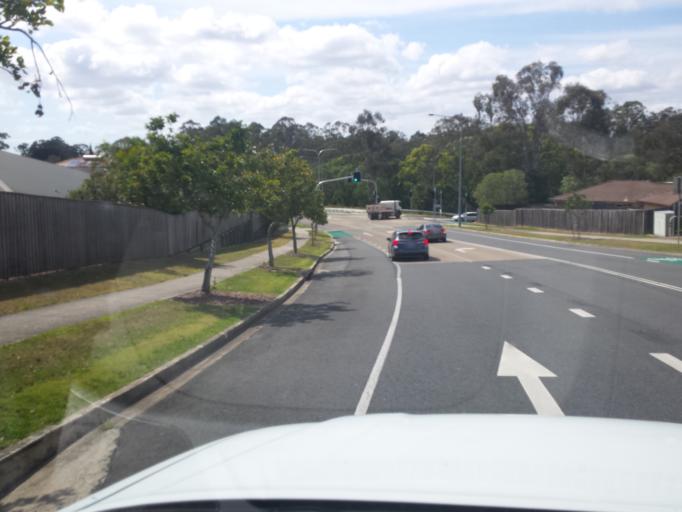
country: AU
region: Queensland
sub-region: Moreton Bay
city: Ferny Hills
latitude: -27.3831
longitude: 152.9619
